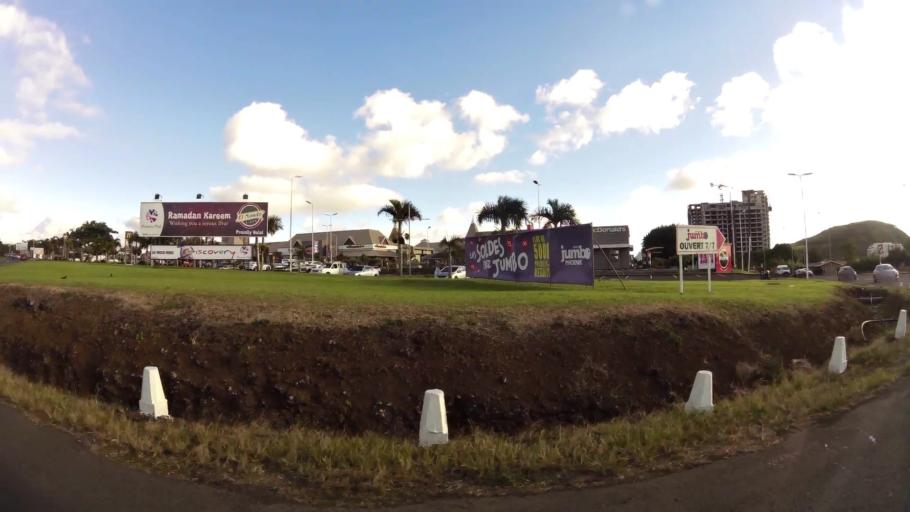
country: MU
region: Plaines Wilhems
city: Quatre Bornes
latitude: -20.2772
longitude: 57.4963
